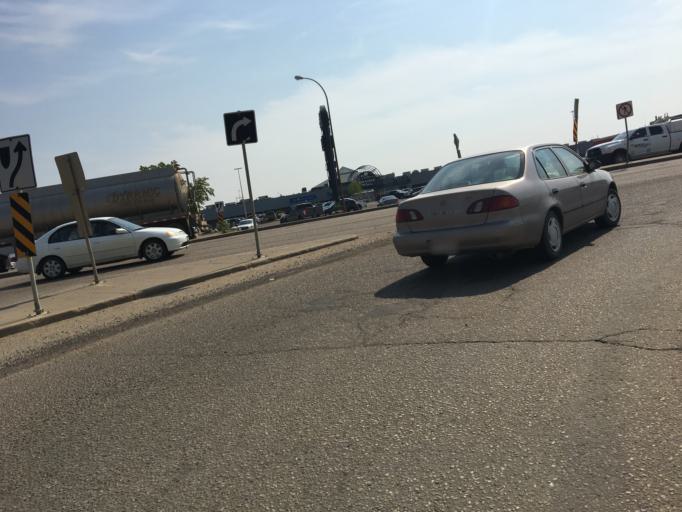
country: CA
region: Alberta
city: Grande Prairie
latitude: 55.1877
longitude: -118.7953
